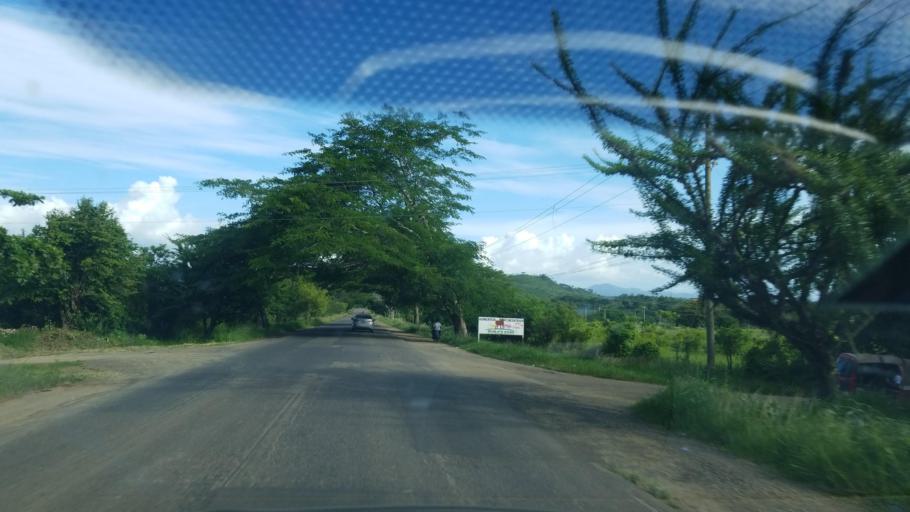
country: HN
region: El Paraiso
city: Arauli
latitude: 13.9538
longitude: -86.5611
